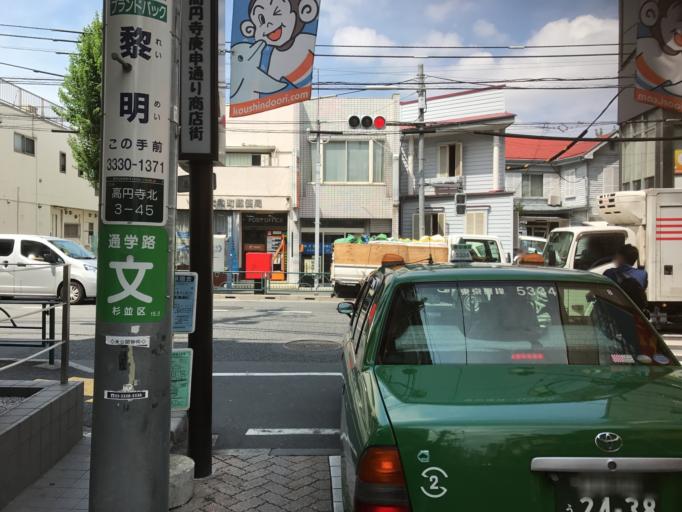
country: JP
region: Tokyo
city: Tokyo
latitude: 35.7098
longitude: 139.6499
